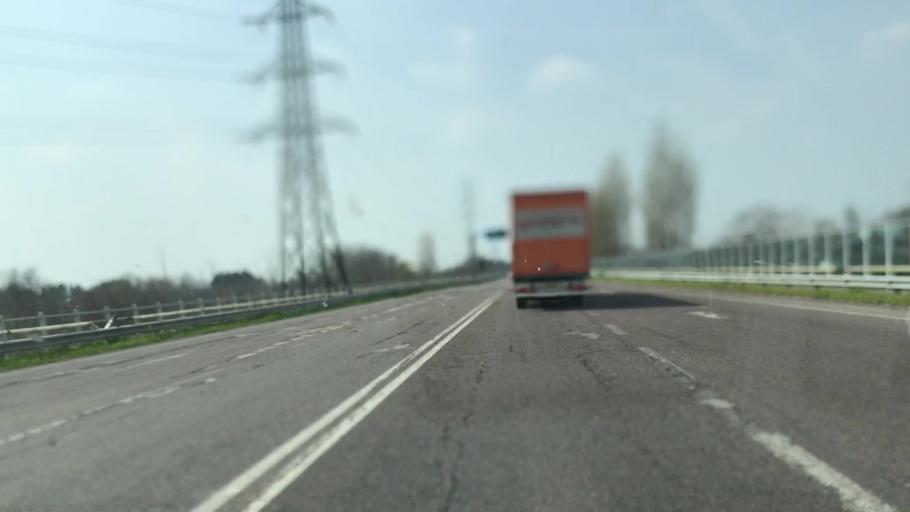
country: IT
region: Lombardy
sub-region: Provincia di Mantova
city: Sant'Antonio
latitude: 45.1856
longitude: 10.7845
